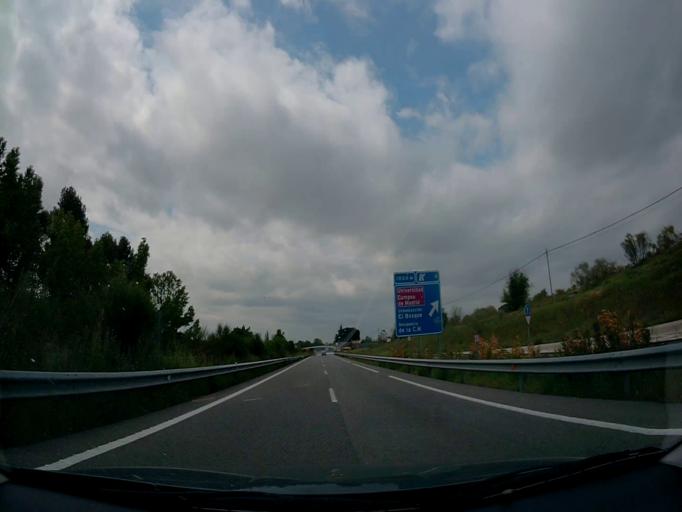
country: ES
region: Madrid
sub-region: Provincia de Madrid
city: Villaviciosa de Odon
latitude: 40.3827
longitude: -3.9055
